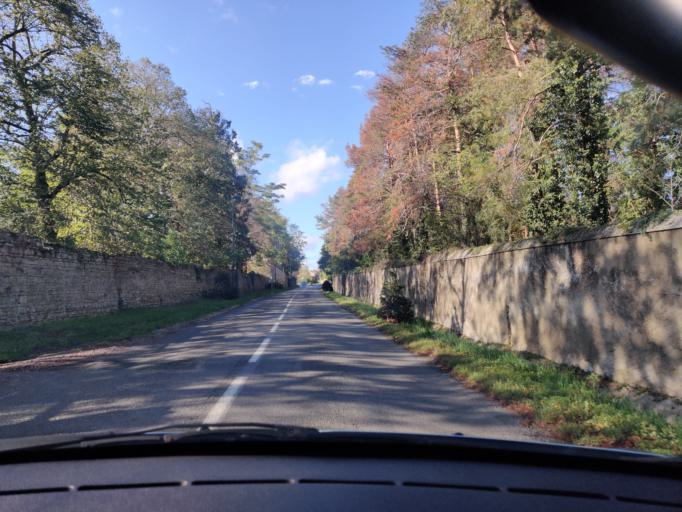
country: FR
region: Auvergne
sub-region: Departement du Puy-de-Dome
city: Combronde
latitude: 45.9944
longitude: 3.1296
